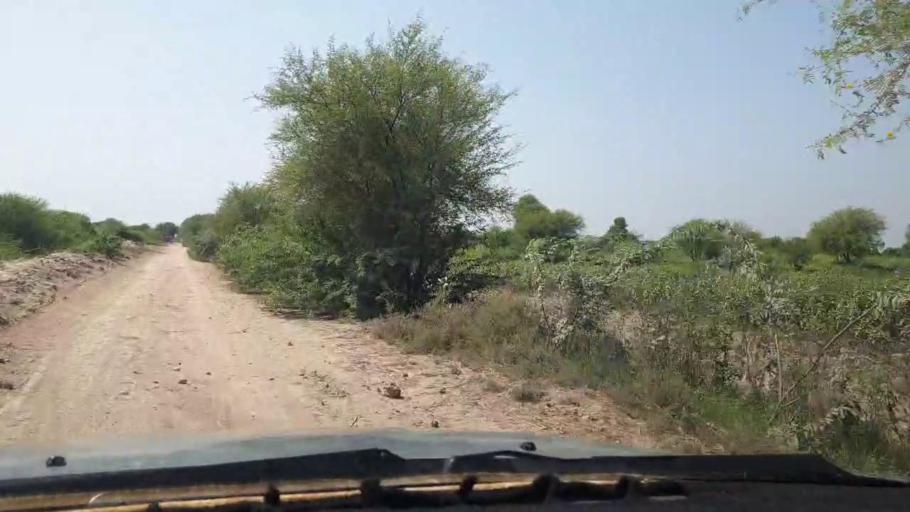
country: PK
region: Sindh
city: Tando Ghulam Ali
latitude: 25.1434
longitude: 68.7906
